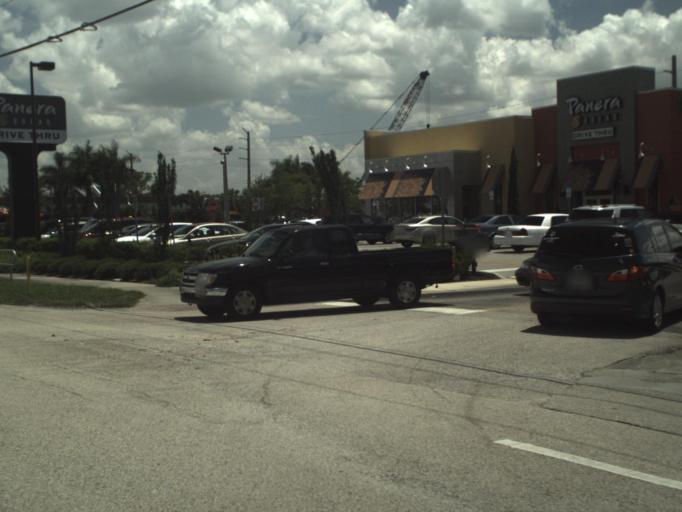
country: US
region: Florida
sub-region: Martin County
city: Port Salerno
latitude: 27.1635
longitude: -80.2257
